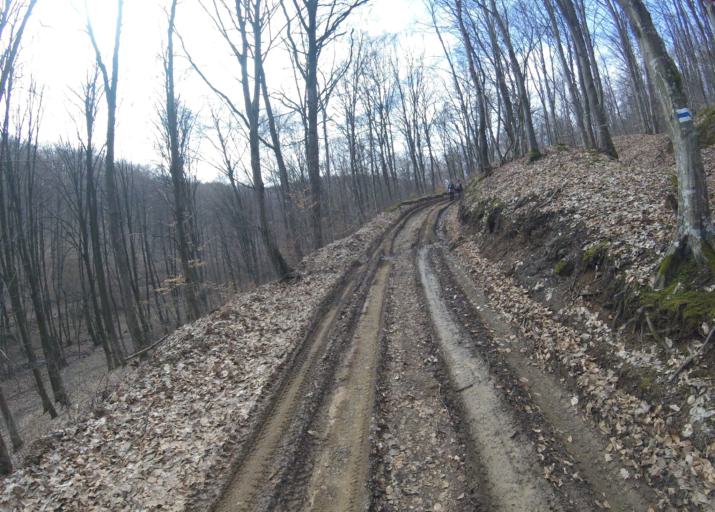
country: HU
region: Heves
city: Belapatfalva
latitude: 48.0184
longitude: 20.3539
